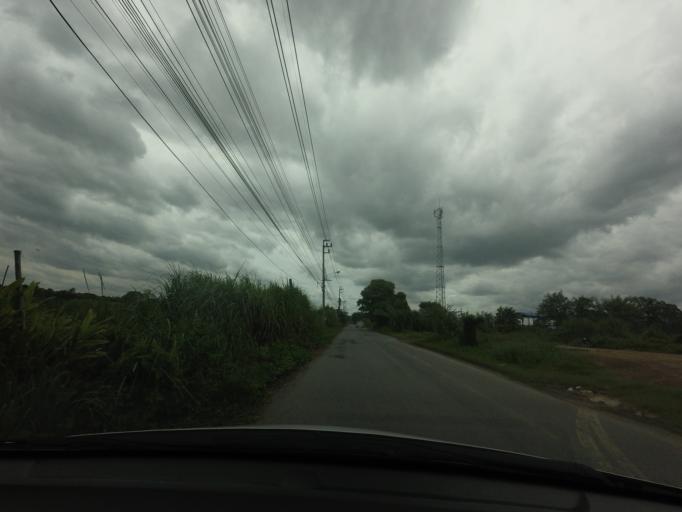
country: TH
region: Bangkok
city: Min Buri
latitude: 13.7752
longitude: 100.7567
